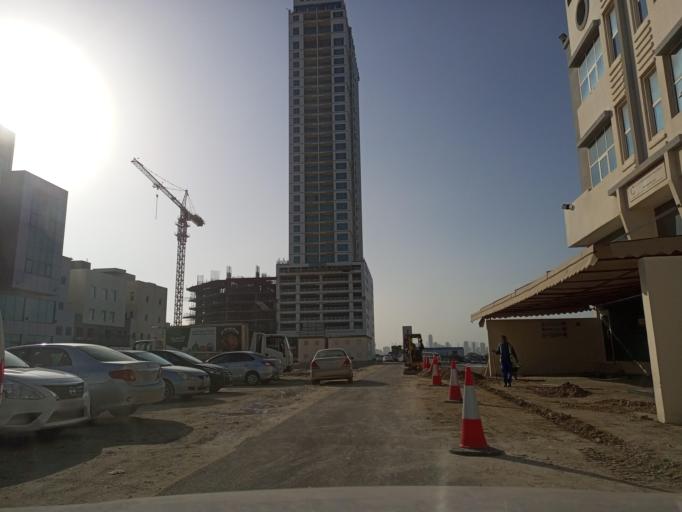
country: BH
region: Muharraq
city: Al Hadd
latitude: 26.2267
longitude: 50.6319
